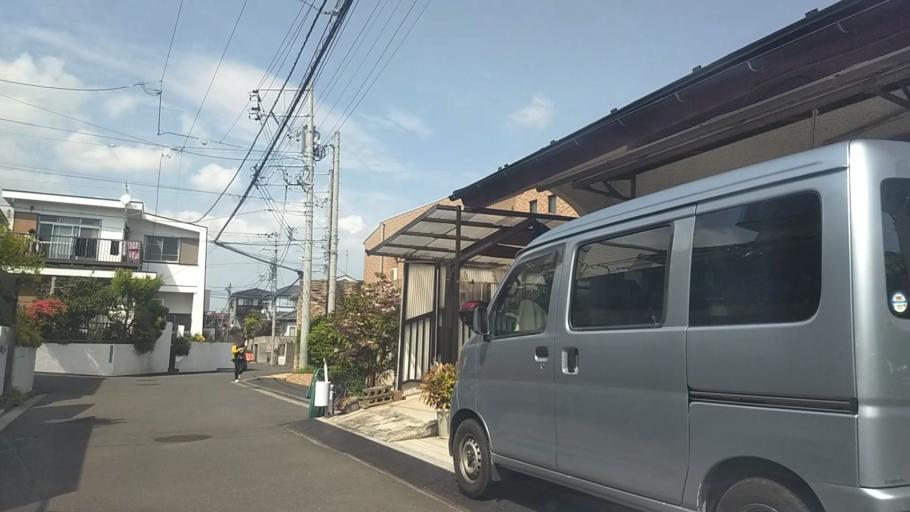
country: JP
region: Kanagawa
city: Kamakura
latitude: 35.3787
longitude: 139.5743
